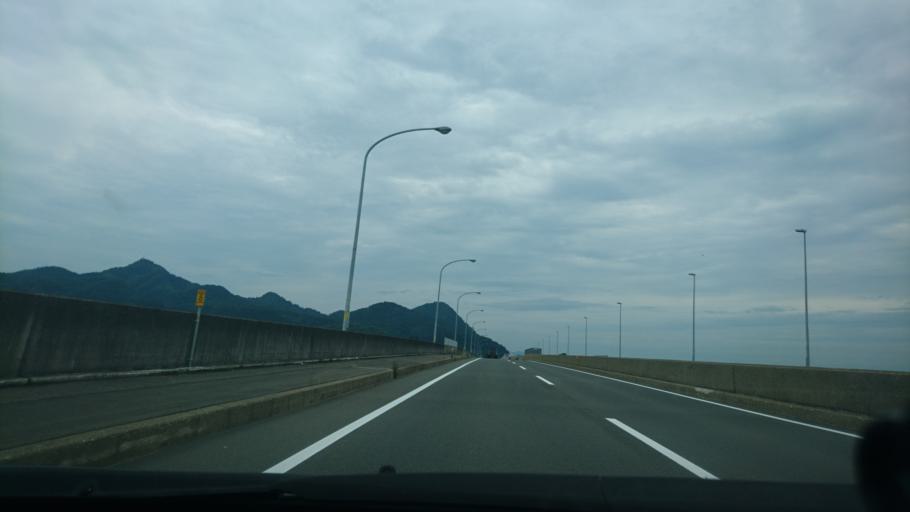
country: JP
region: Akita
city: Omagari
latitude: 39.4762
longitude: 140.4695
